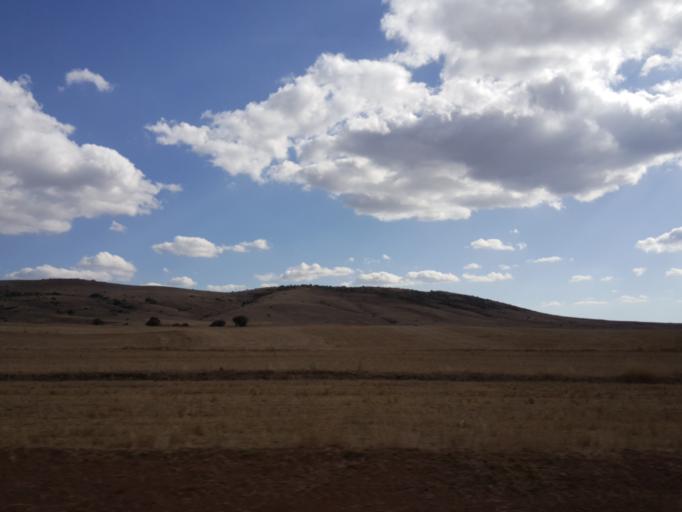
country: TR
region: Tokat
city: Sulusaray
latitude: 39.9864
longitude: 35.9555
